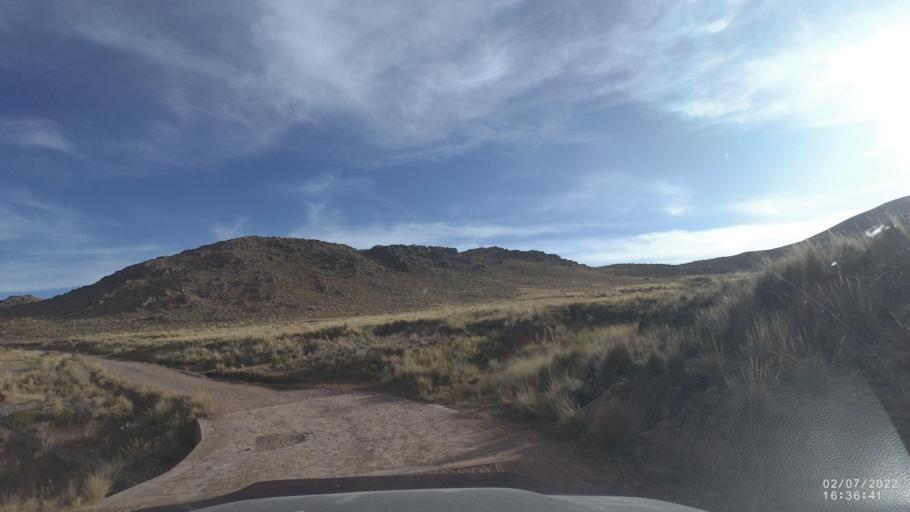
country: BO
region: Cochabamba
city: Irpa Irpa
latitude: -17.9638
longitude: -66.4961
